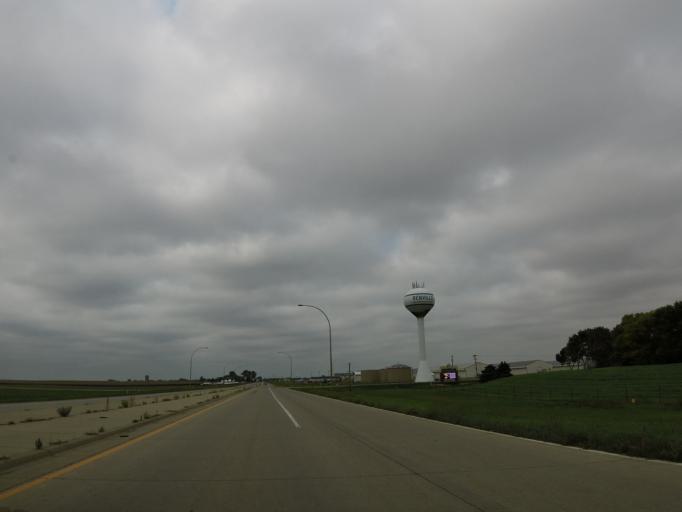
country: US
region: Minnesota
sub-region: Renville County
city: Renville
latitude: 44.7892
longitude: -95.1769
